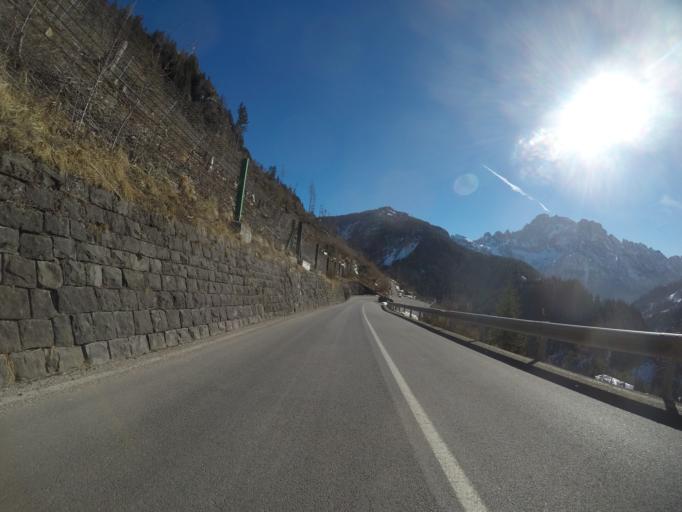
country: IT
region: Veneto
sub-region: Provincia di Belluno
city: Colle Santa Lucia
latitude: 46.4427
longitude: 11.9968
